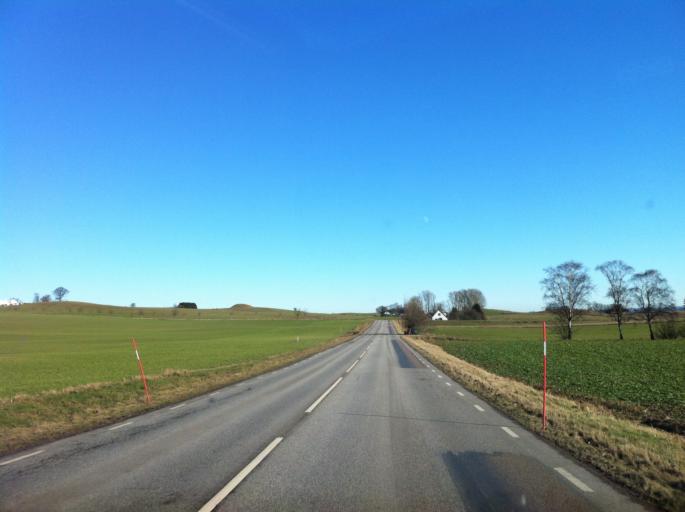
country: SE
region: Skane
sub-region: Svedala Kommun
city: Klagerup
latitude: 55.5774
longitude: 13.1943
